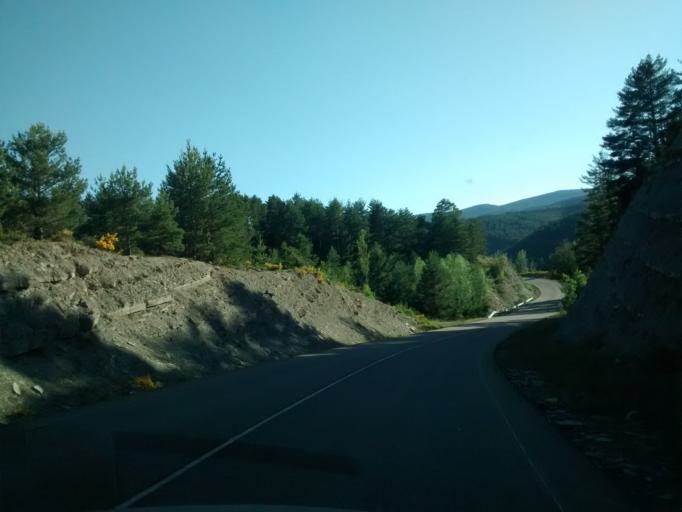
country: ES
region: Aragon
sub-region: Provincia de Huesca
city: Borau
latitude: 42.6673
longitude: -0.6218
